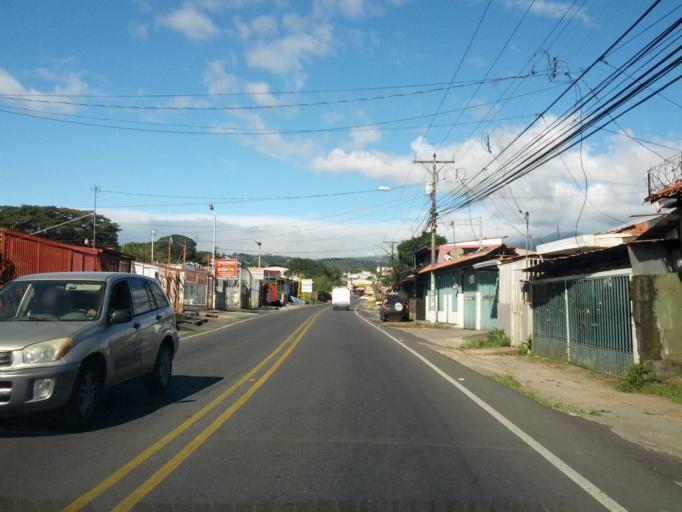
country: CR
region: Alajuela
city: Alajuela
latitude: 10.0217
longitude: -84.2071
